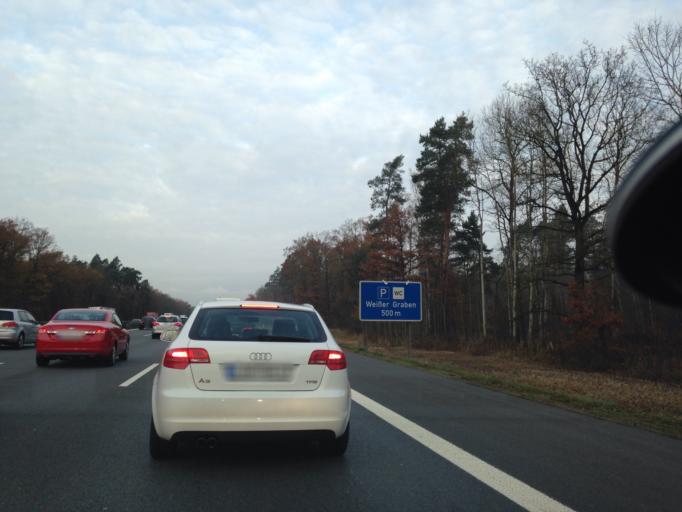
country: DE
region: Bavaria
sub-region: Regierungsbezirk Mittelfranken
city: Wetzendorf
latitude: 49.5207
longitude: 11.0778
